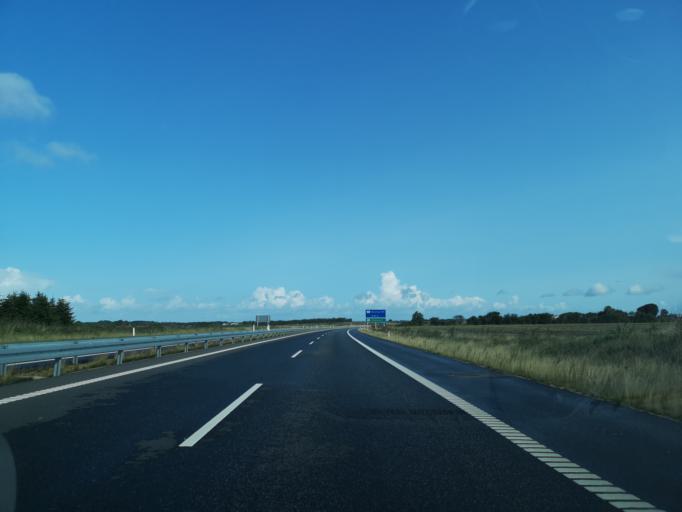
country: DK
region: Central Jutland
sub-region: Herning Kommune
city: Snejbjerg
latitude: 56.1389
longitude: 8.8696
